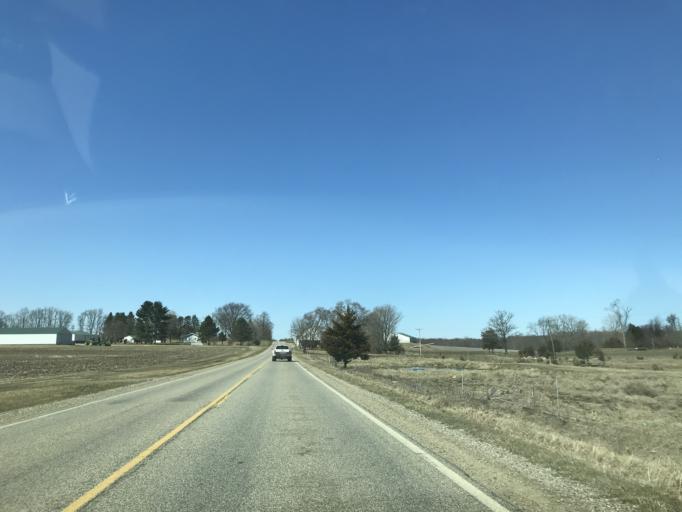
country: US
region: Michigan
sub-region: Hillsdale County
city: Litchfield
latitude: 41.9857
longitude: -84.7949
